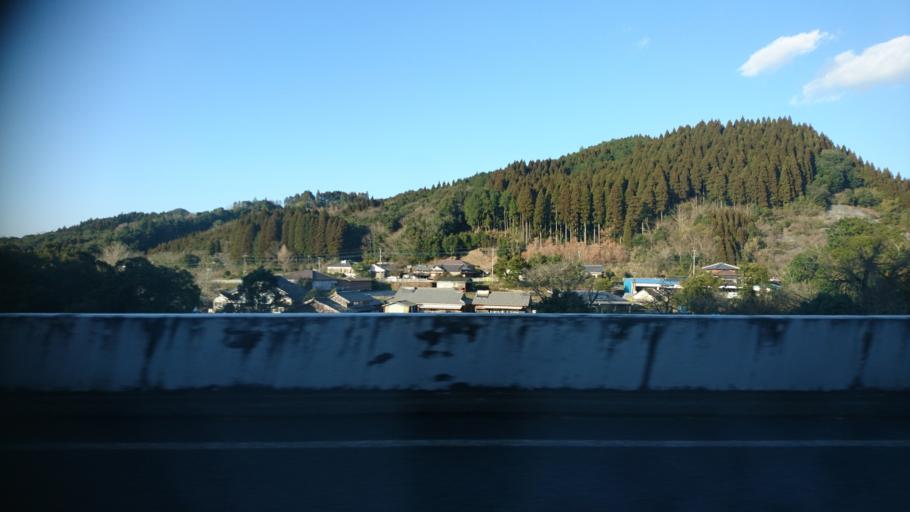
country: JP
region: Miyazaki
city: Miyakonojo
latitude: 31.7920
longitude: 131.1800
